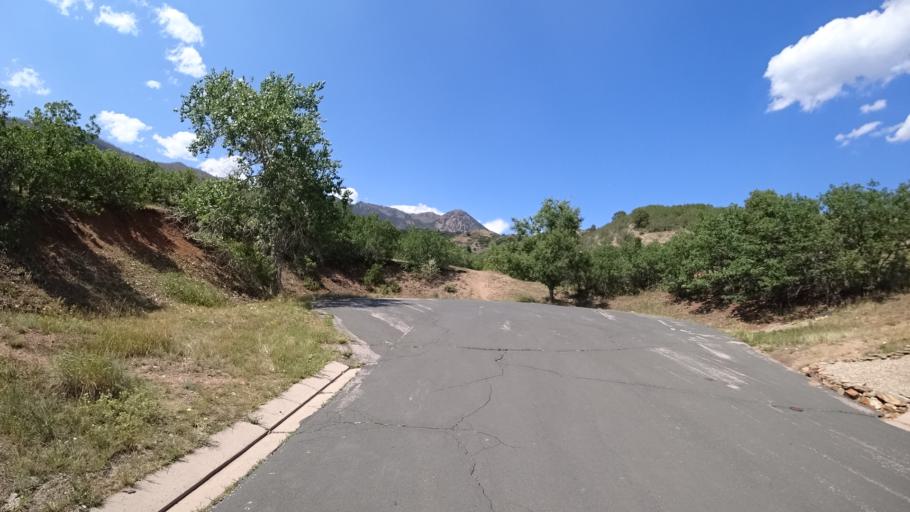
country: US
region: Colorado
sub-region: El Paso County
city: Air Force Academy
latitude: 38.9385
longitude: -104.8820
